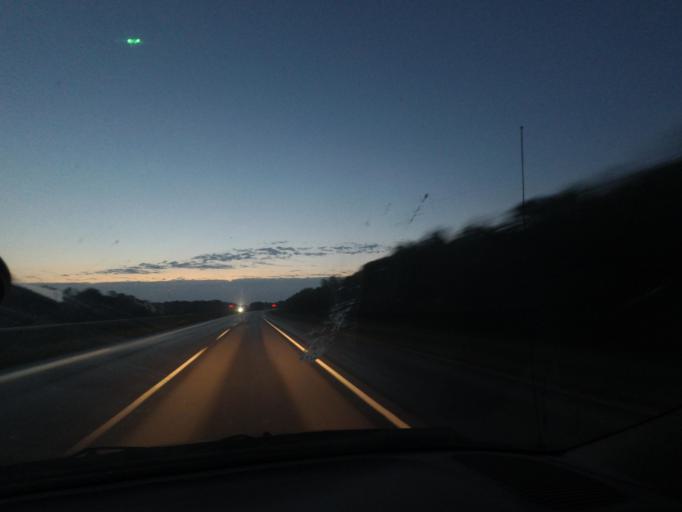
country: US
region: Missouri
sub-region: Linn County
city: Linneus
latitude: 39.7777
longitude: -93.3220
